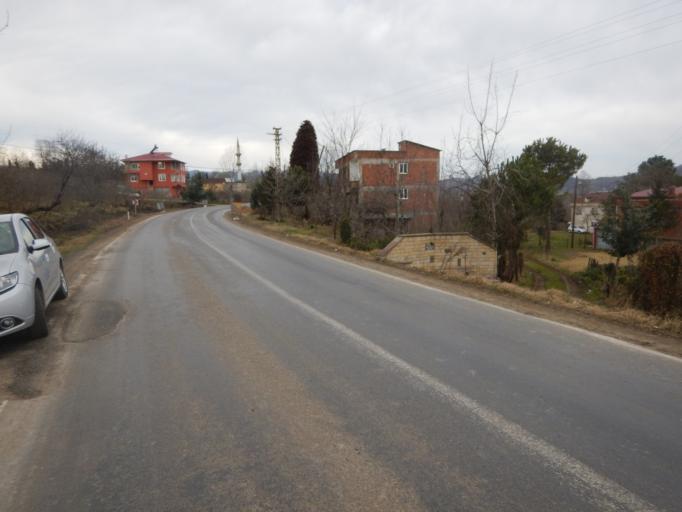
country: TR
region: Ordu
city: Uzunisa
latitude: 40.9020
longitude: 37.8171
